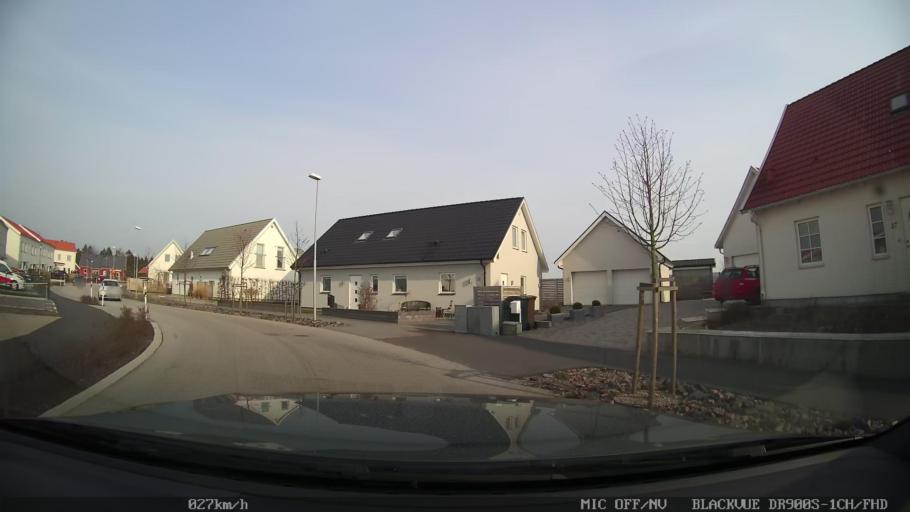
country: SE
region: Skane
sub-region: Ystads Kommun
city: Ystad
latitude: 55.4431
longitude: 13.7973
